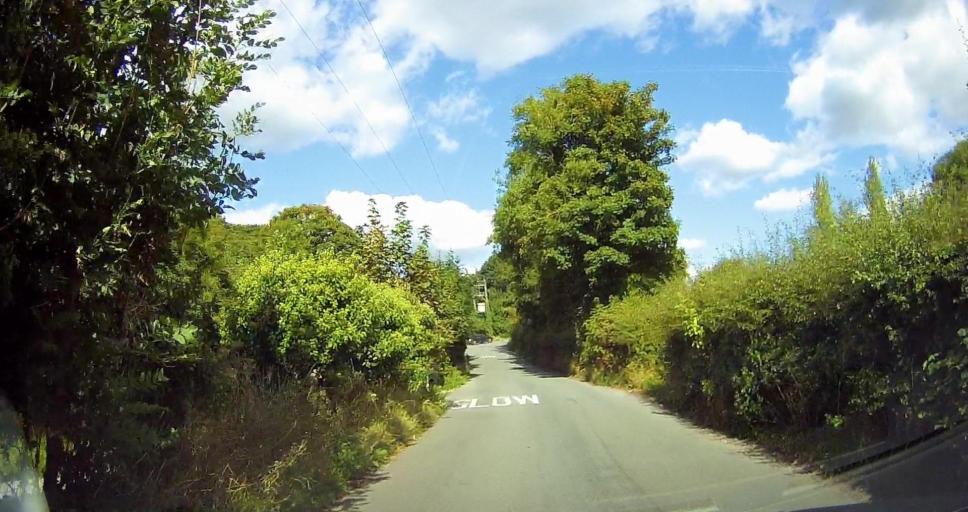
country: GB
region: England
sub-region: Staffordshire
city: Stone
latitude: 52.9174
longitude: -2.1630
